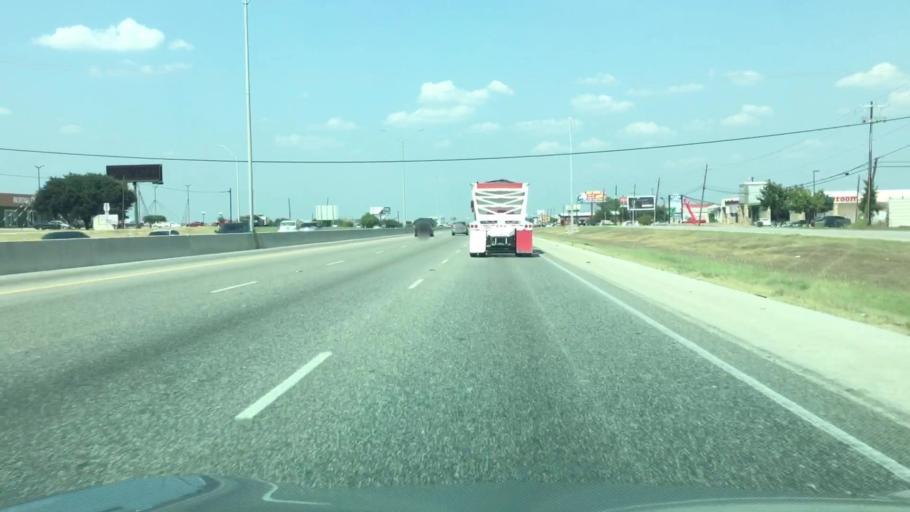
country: US
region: Texas
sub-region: Hays County
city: San Marcos
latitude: 29.8475
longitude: -97.9631
